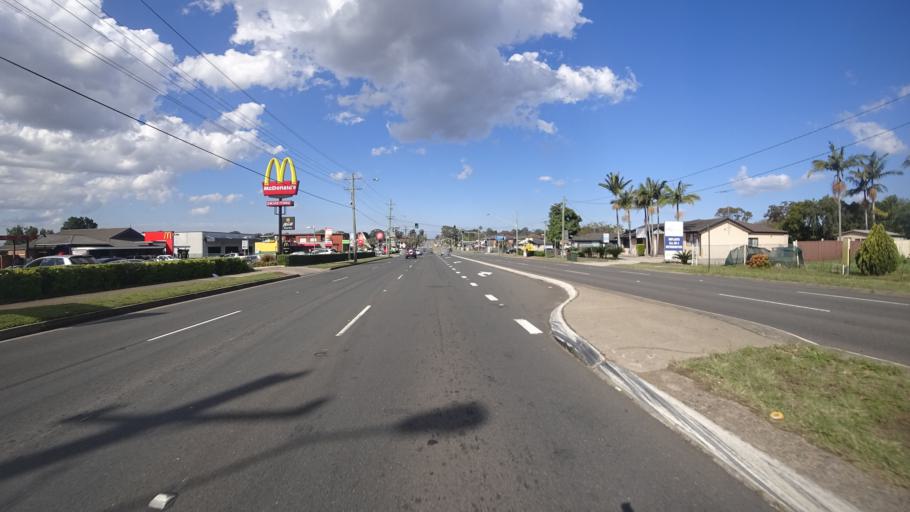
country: AU
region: New South Wales
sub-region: Fairfield
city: Chipping Norton
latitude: -33.9291
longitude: 150.9467
